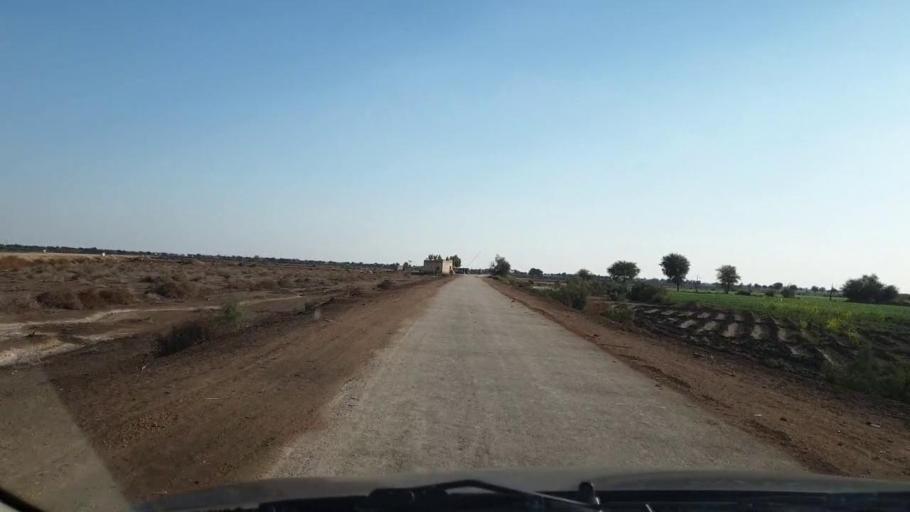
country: PK
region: Sindh
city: Sinjhoro
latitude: 26.0073
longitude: 68.8382
